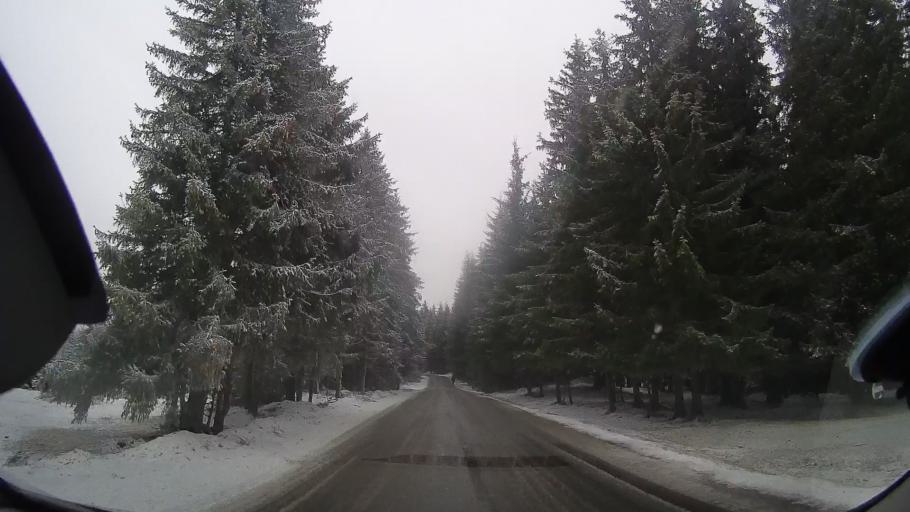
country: RO
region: Cluj
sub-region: Comuna Belis
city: Belis
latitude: 46.6386
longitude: 23.0519
